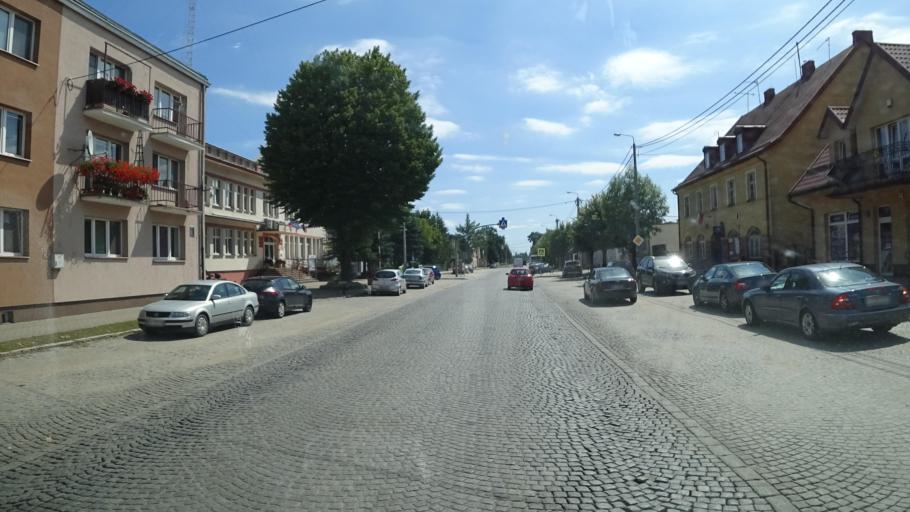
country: PL
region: Warmian-Masurian Voivodeship
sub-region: Powiat elcki
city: Prostki
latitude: 53.6971
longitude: 22.4355
